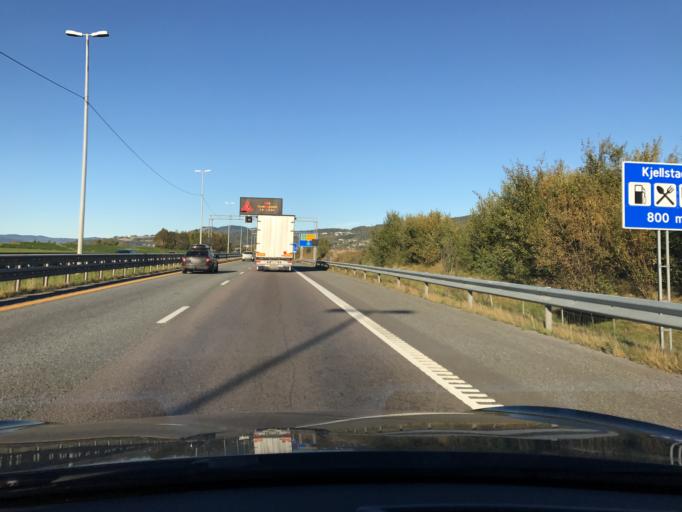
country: NO
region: Buskerud
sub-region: Lier
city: Lierbyen
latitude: 59.7573
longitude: 10.2498
